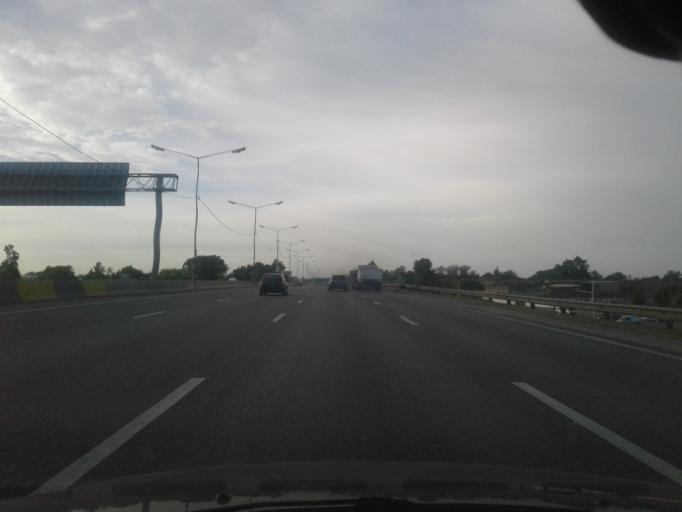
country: AR
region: Santa Fe
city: Perez
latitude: -32.9395
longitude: -60.7227
